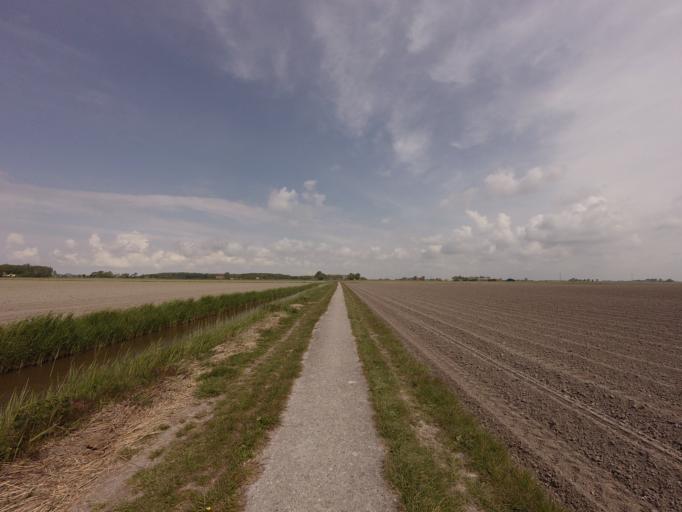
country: NL
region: Friesland
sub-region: Sudwest Fryslan
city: Bolsward
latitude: 53.1040
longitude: 5.4851
